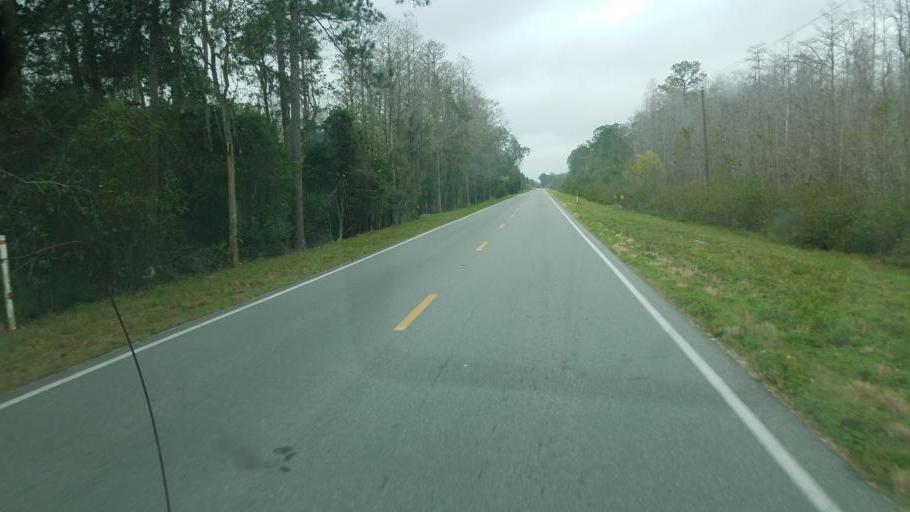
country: US
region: Florida
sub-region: Polk County
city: Polk City
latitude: 28.2589
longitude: -81.7741
